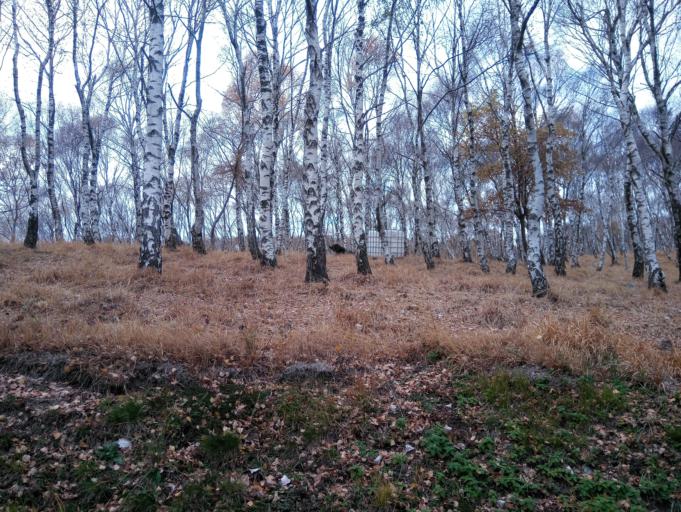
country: CH
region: Ticino
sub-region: Bellinzona District
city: Cadenazzo
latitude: 46.1311
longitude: 8.9603
